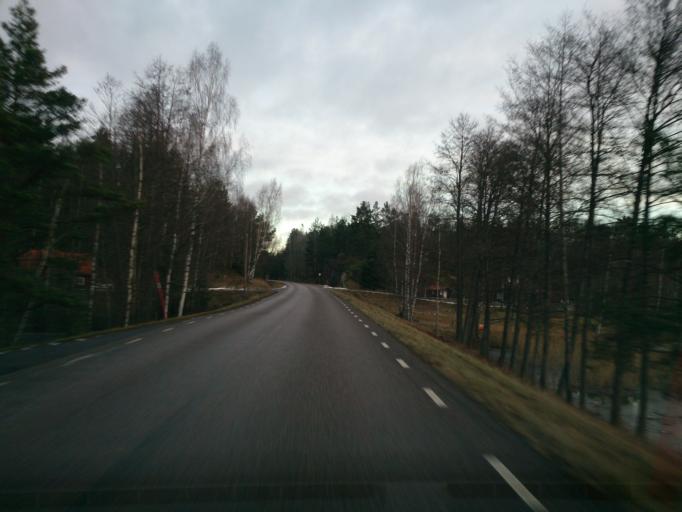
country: SE
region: OEstergoetland
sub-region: Atvidabergs Kommun
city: Atvidaberg
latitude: 58.2436
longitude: 16.0097
